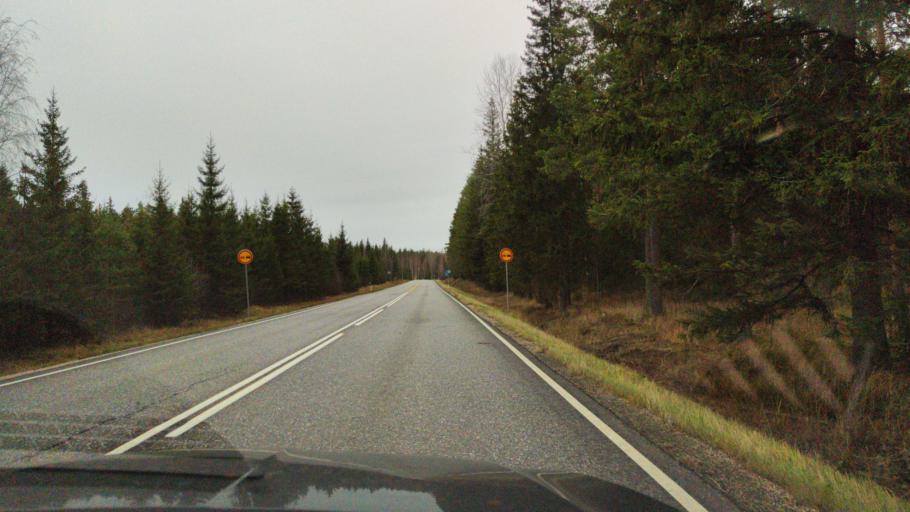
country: FI
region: Varsinais-Suomi
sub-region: Loimaa
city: Ylaene
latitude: 60.7364
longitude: 22.4315
